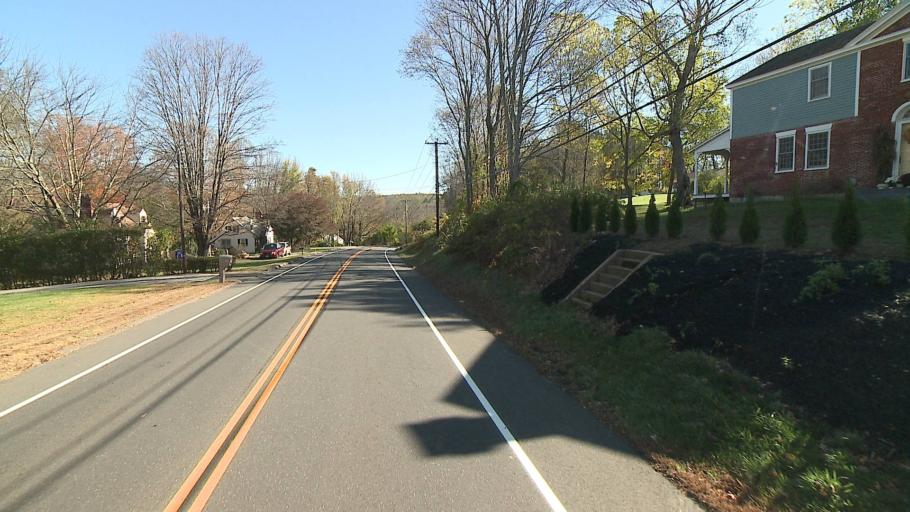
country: US
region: Connecticut
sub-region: Tolland County
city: Coventry Lake
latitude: 41.7995
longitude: -72.3549
